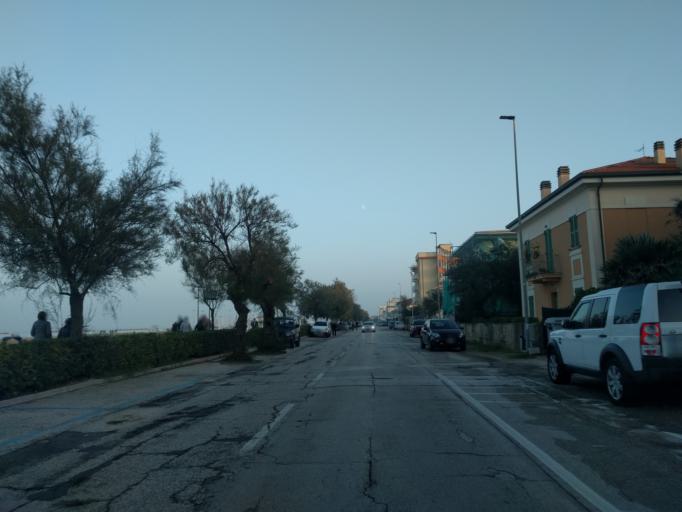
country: IT
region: The Marches
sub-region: Provincia di Ancona
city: Senigallia
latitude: 43.7296
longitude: 13.2021
